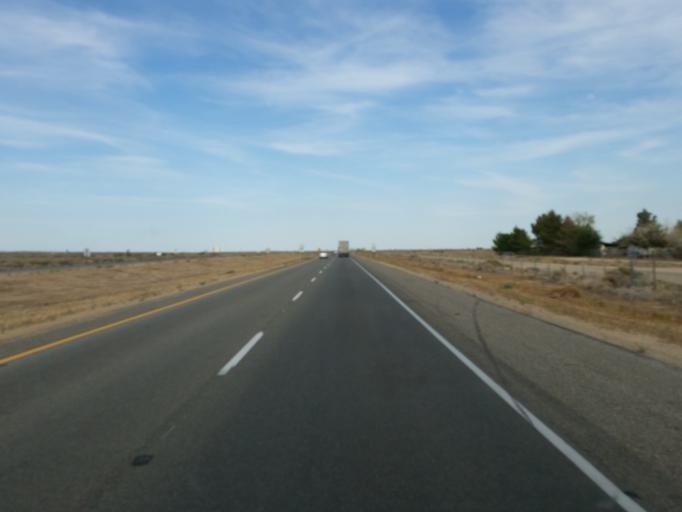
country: US
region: California
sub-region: Kern County
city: Boron
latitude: 35.0101
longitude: -117.6377
